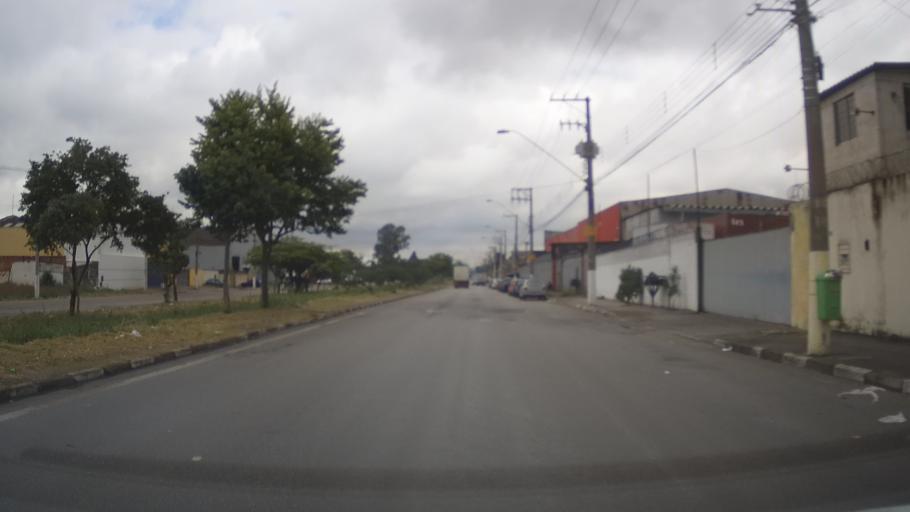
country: BR
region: Sao Paulo
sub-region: Guarulhos
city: Guarulhos
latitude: -23.4657
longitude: -46.4736
